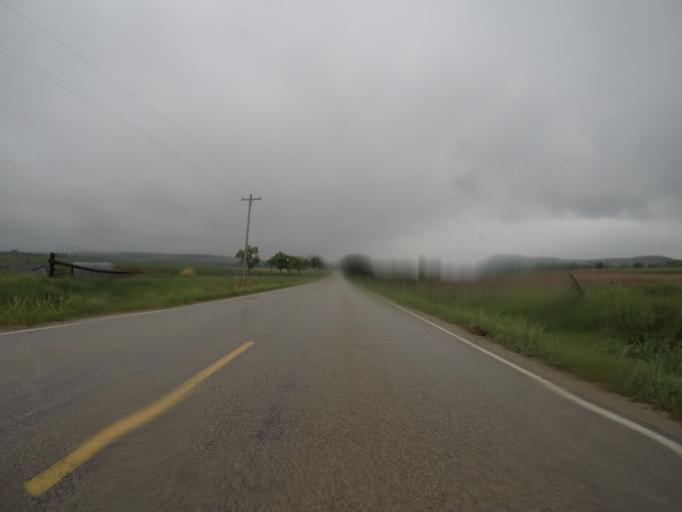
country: US
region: Kansas
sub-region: Pottawatomie County
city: Westmoreland
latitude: 39.4047
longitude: -96.1839
